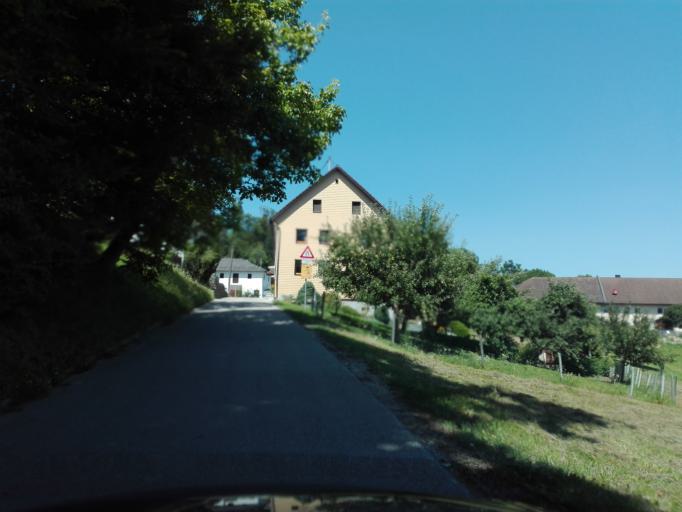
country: AT
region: Upper Austria
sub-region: Politischer Bezirk Urfahr-Umgebung
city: Gallneukirchen
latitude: 48.3233
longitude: 14.3982
